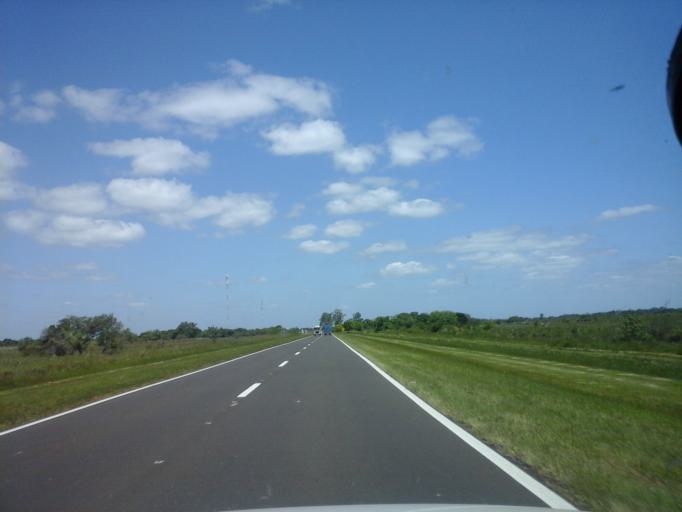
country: PY
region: Neembucu
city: Cerrito
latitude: -27.3838
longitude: -57.8077
